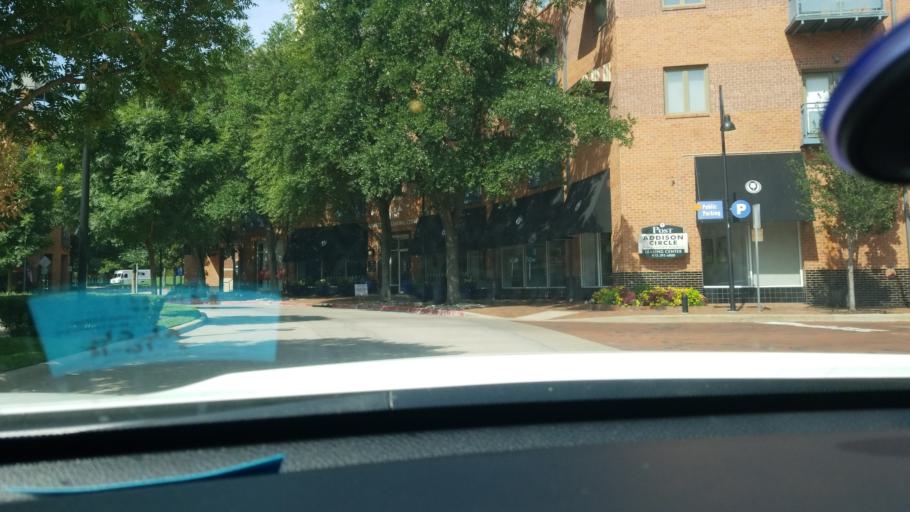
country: US
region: Texas
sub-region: Dallas County
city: Addison
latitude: 32.9619
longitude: -96.8246
